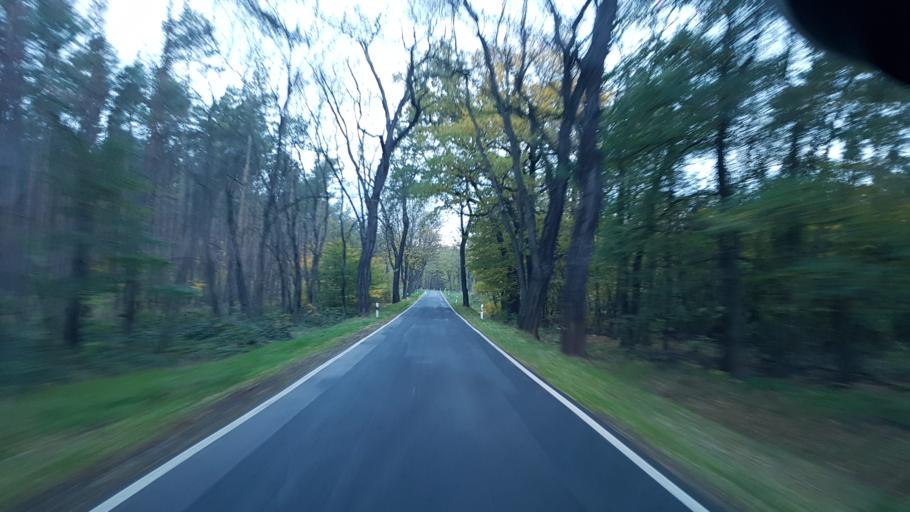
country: DE
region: Brandenburg
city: Muhlberg
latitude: 51.4798
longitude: 13.2346
